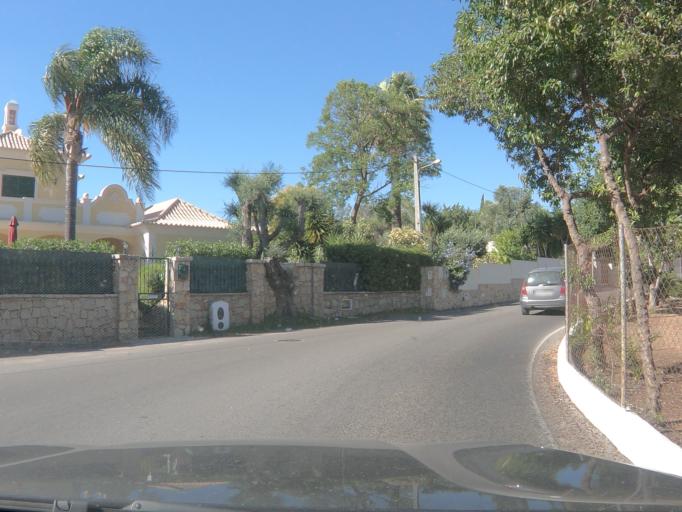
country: PT
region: Faro
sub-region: Loule
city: Almancil
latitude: 37.1097
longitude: -8.0344
